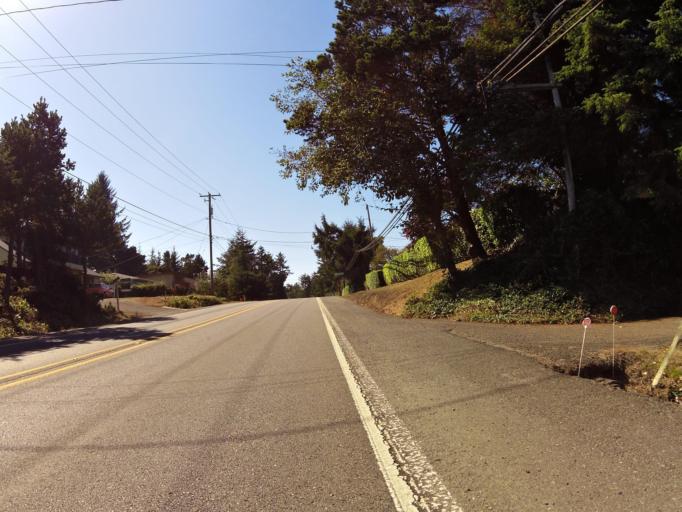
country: US
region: Oregon
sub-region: Coos County
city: Barview
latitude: 43.3575
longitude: -124.3093
